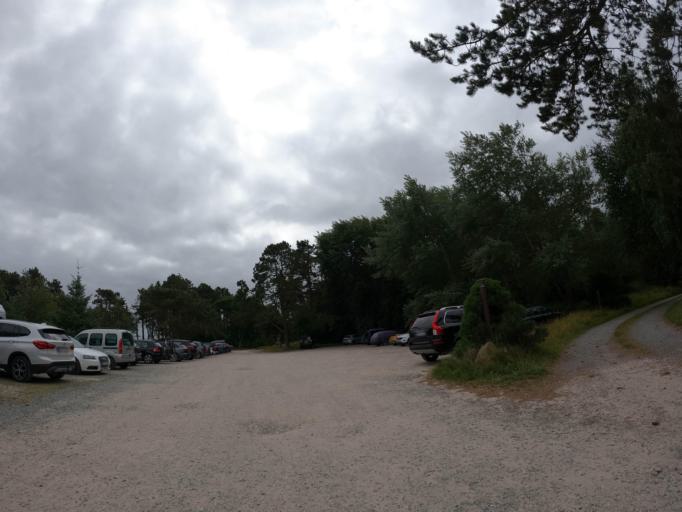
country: DE
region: Schleswig-Holstein
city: Tinnum
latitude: 54.9531
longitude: 8.3529
